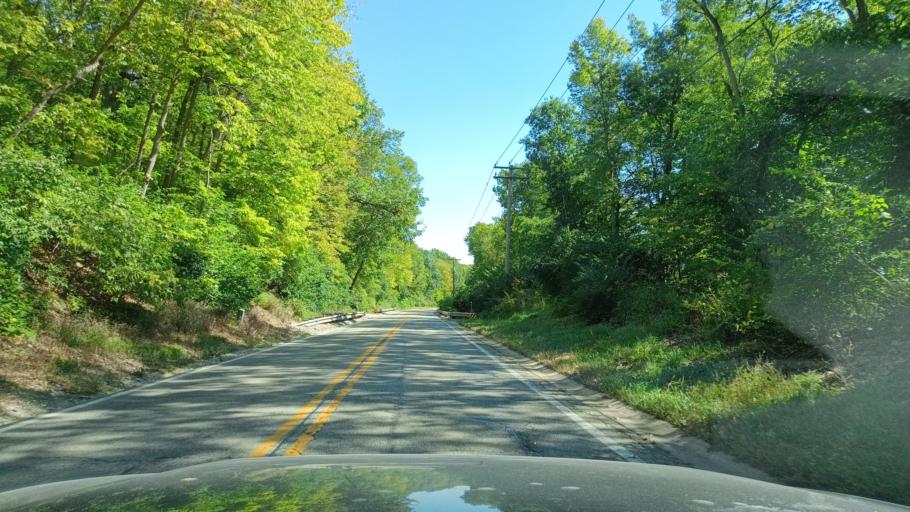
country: US
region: Illinois
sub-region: Woodford County
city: Eureka
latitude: 40.6273
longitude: -89.2514
